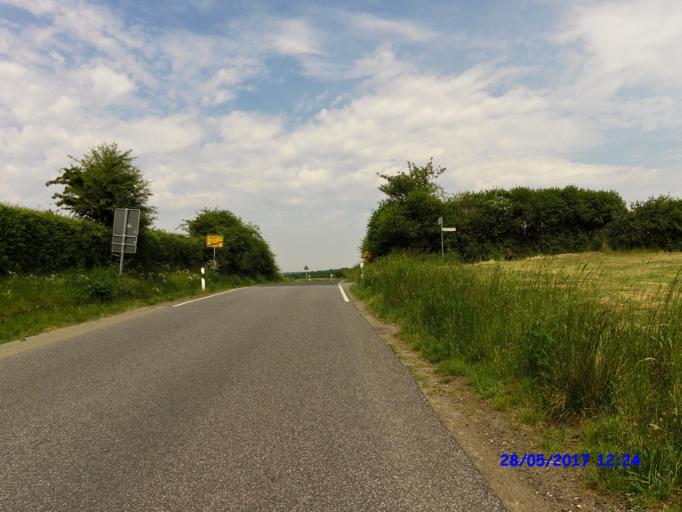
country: DE
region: Rheinland-Pfalz
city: Berg
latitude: 50.5580
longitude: 6.9473
